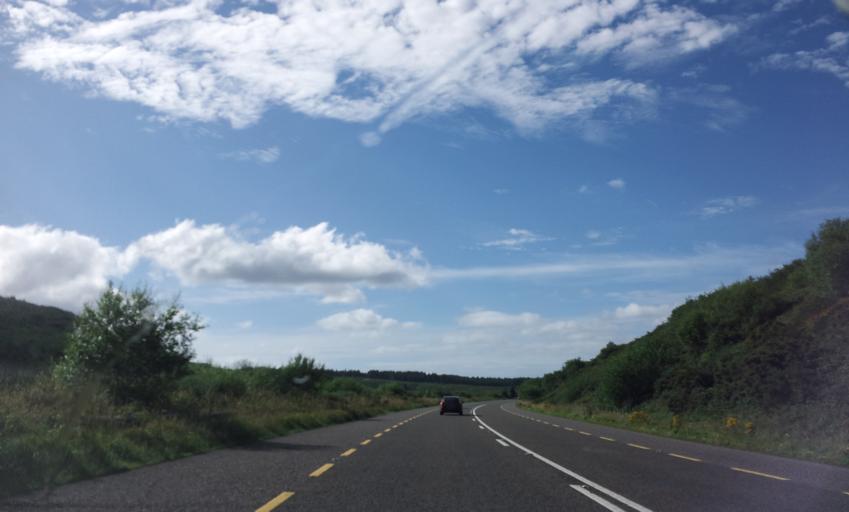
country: IE
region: Munster
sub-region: County Cork
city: Millstreet
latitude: 51.9614
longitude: -9.2408
